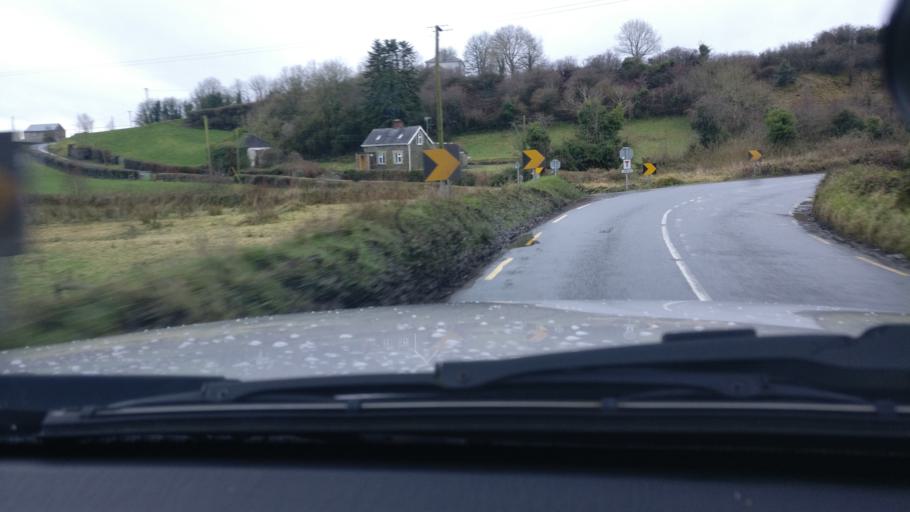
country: IE
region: Leinster
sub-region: An Longfort
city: Granard
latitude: 53.8044
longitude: -7.3793
